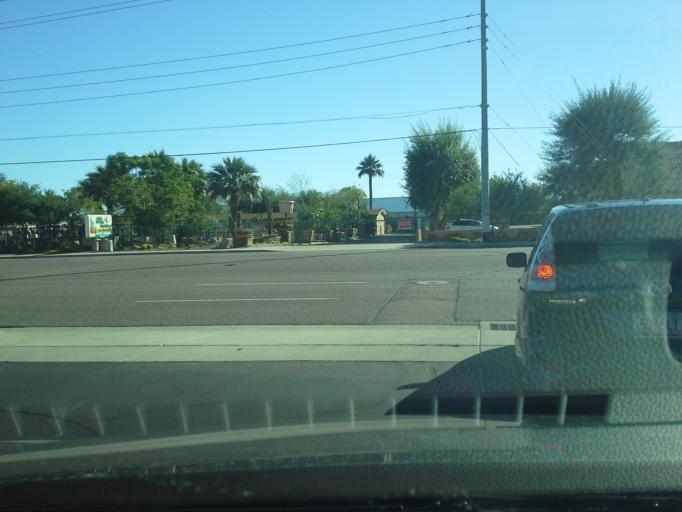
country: US
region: Arizona
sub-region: Maricopa County
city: Paradise Valley
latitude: 33.6409
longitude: -111.9923
